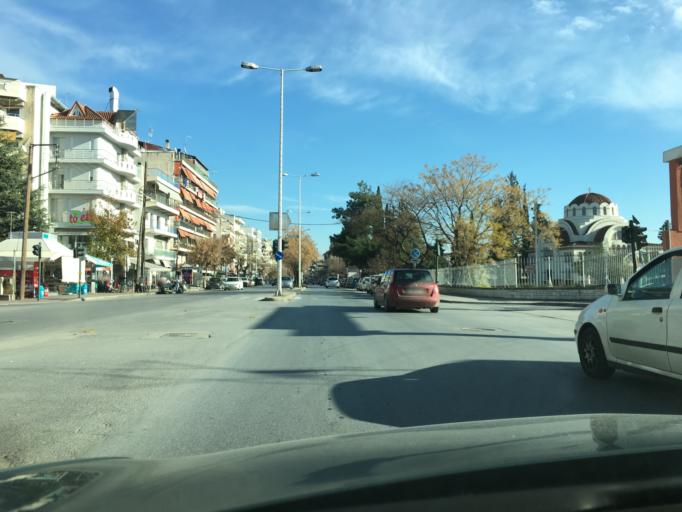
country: GR
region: Thessaly
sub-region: Nomos Larisis
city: Larisa
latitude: 39.6327
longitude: 22.4089
